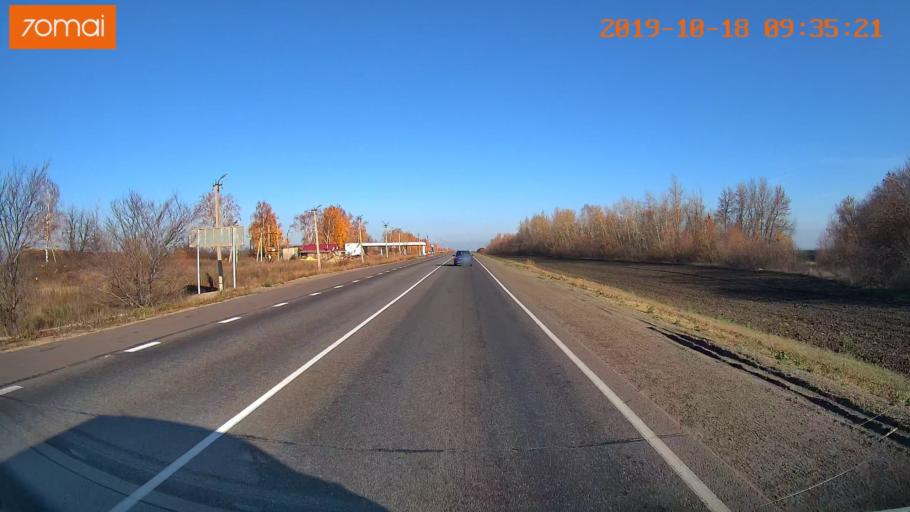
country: RU
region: Tula
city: Yefremov
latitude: 53.1913
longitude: 38.1488
